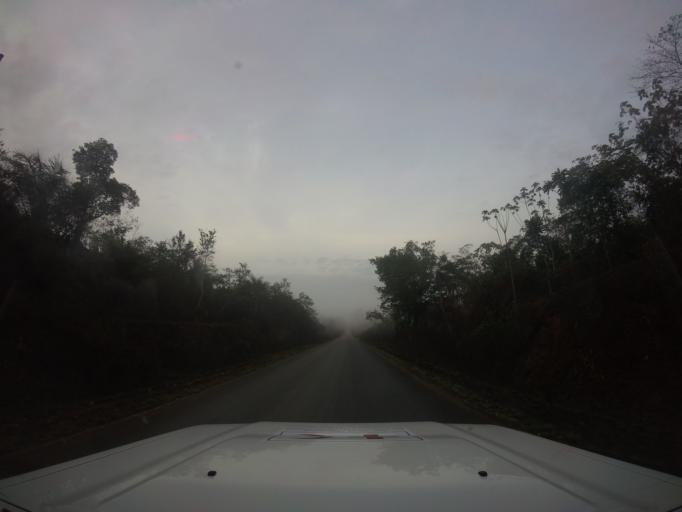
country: LR
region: Bomi
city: Tubmanburg
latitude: 6.7401
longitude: -10.8575
